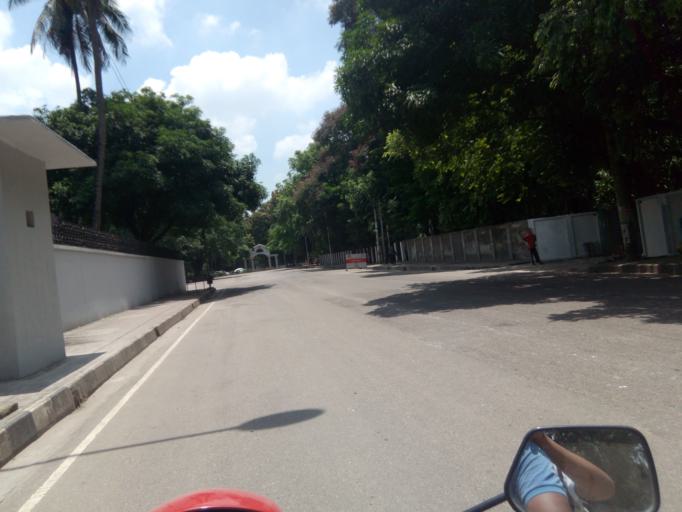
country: BD
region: Dhaka
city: Paltan
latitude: 23.7407
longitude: 90.4018
